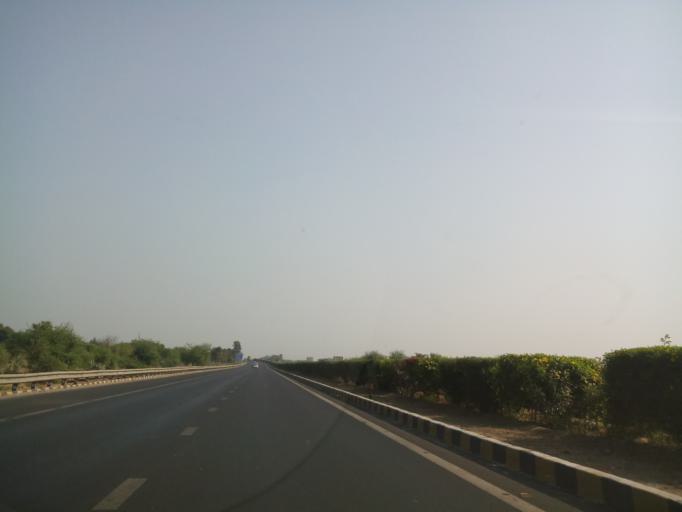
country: IN
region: Gujarat
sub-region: Ahmadabad
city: Ahmedabad
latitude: 22.9662
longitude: 72.6673
